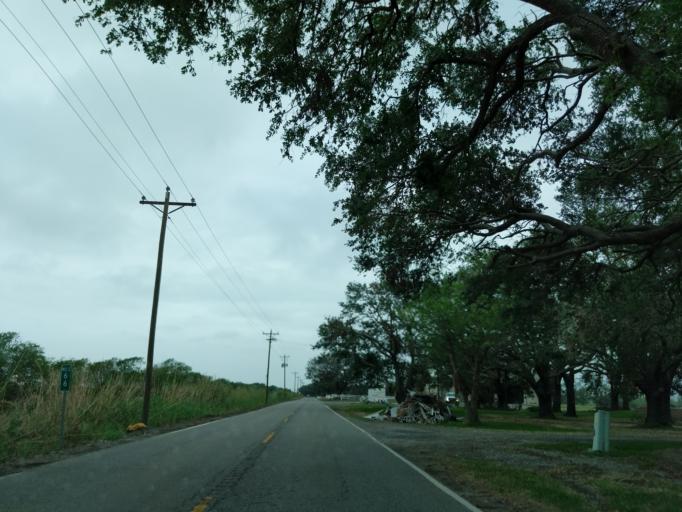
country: US
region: Louisiana
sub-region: Jefferson Davis Parish
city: Lake Arthur
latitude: 29.7510
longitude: -92.9048
